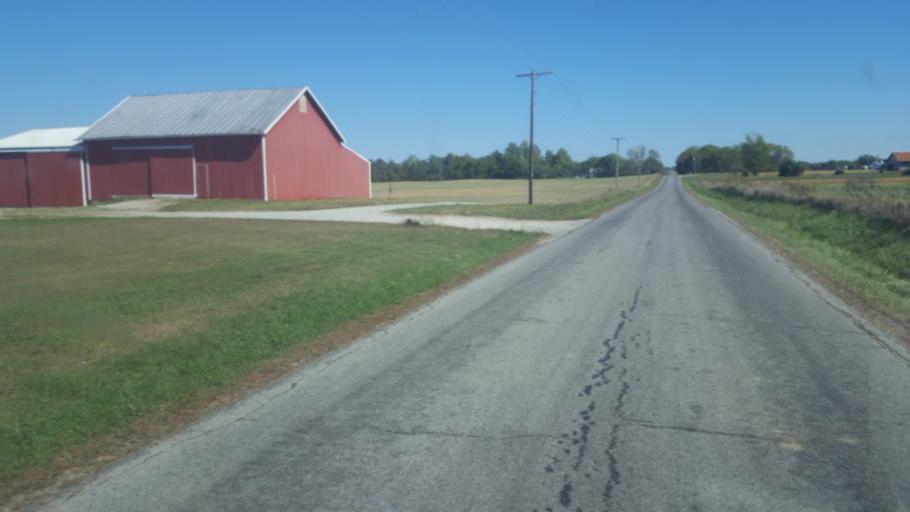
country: US
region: Ohio
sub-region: Huron County
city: Greenwich
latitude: 40.9934
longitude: -82.5335
